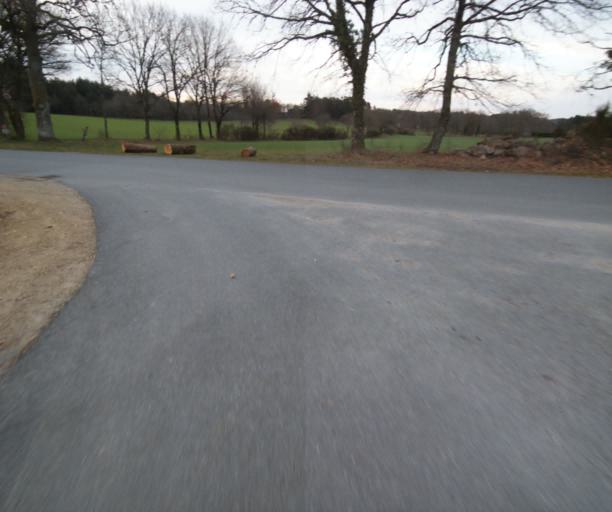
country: FR
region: Limousin
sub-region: Departement de la Correze
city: Correze
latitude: 45.4294
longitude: 1.8371
